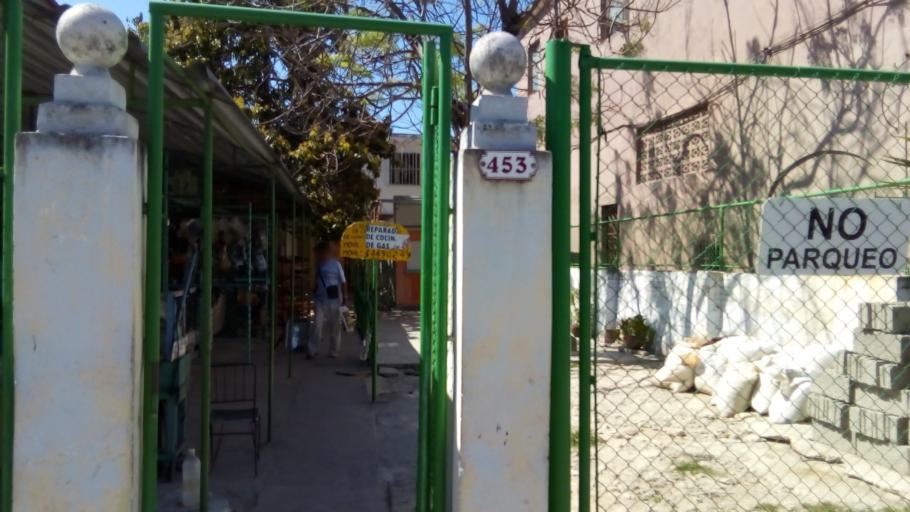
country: CU
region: La Habana
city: Diez de Octubre
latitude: 23.0893
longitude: -82.3763
